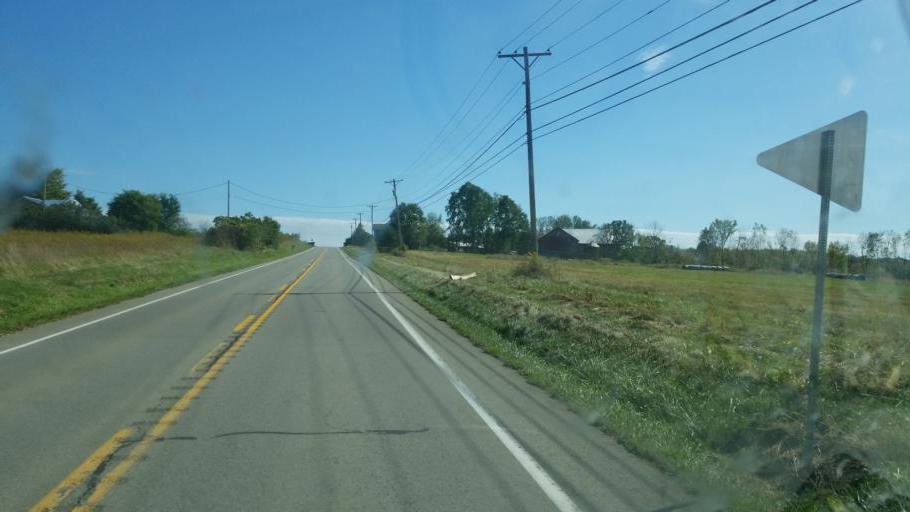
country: US
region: Pennsylvania
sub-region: Mercer County
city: Reynolds Heights
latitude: 41.3362
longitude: -80.3231
